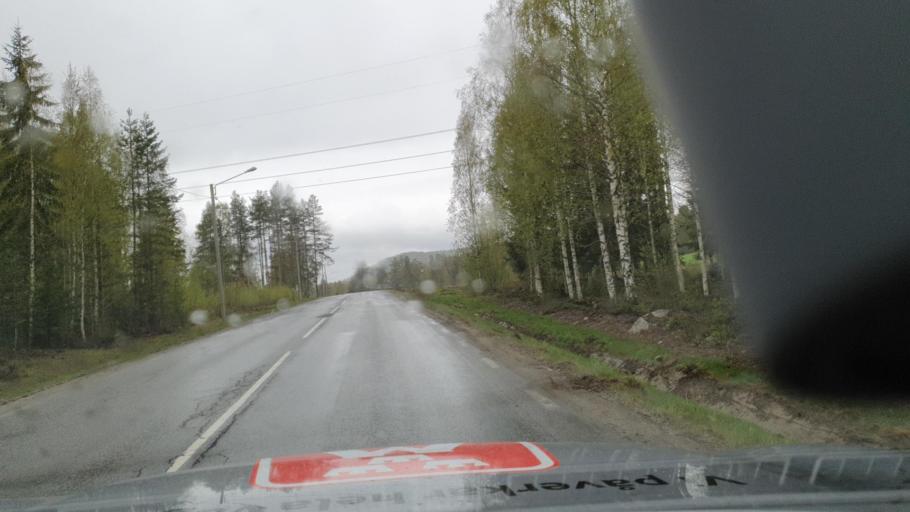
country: SE
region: Vaesternorrland
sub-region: OErnskoeldsviks Kommun
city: Bredbyn
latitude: 63.4691
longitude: 17.9500
